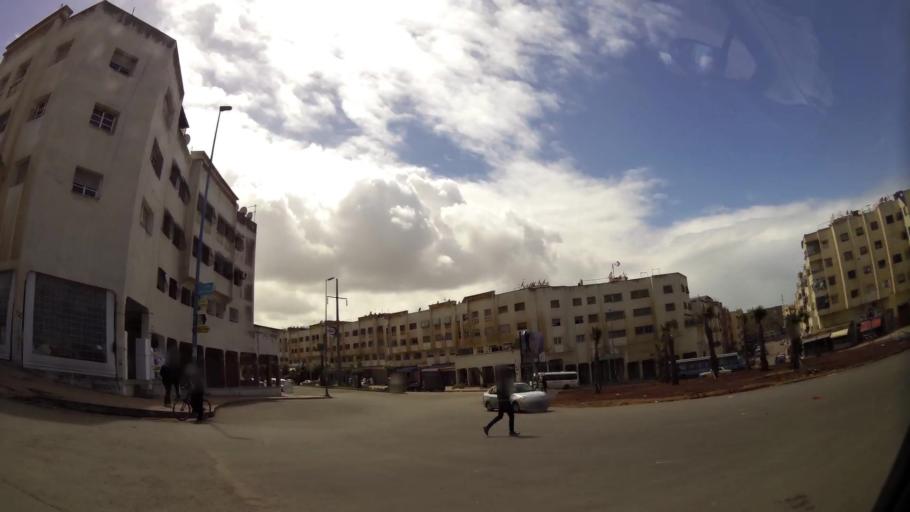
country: MA
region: Grand Casablanca
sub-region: Mediouna
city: Tit Mellil
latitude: 33.6040
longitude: -7.4817
